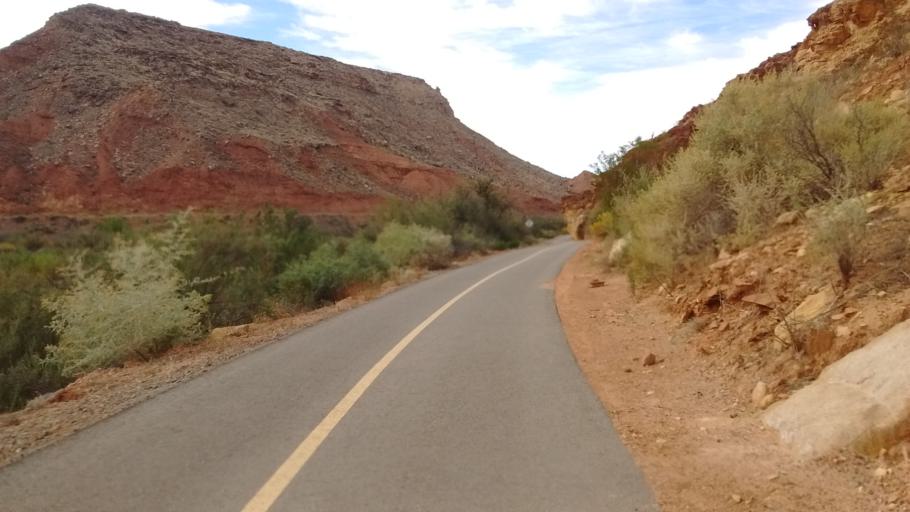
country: US
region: Utah
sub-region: Washington County
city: Washington
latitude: 37.1222
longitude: -113.4793
